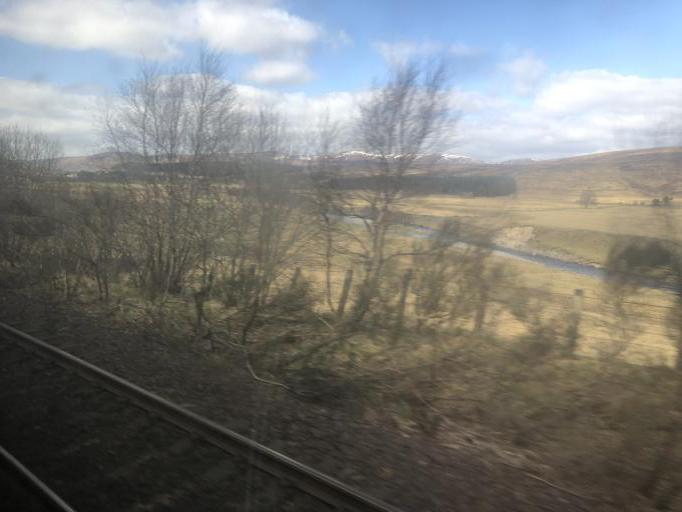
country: GB
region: Scotland
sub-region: Perth and Kinross
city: Aberfeldy
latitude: 56.7982
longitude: -4.0580
